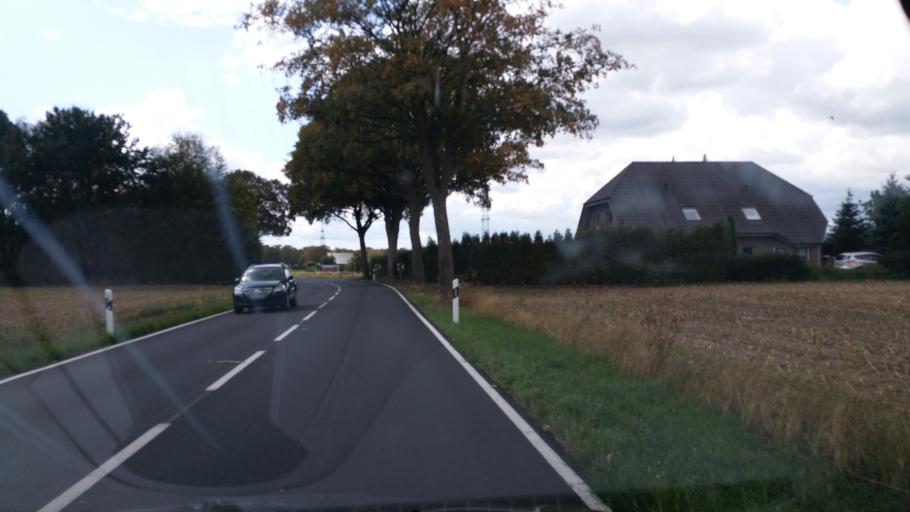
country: DE
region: North Rhine-Westphalia
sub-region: Regierungsbezirk Dusseldorf
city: Hamminkeln
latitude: 51.7185
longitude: 6.5858
